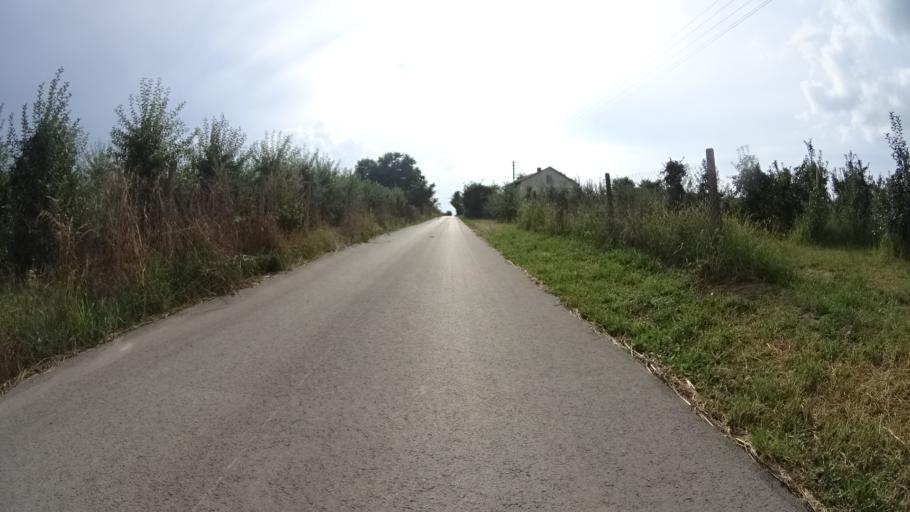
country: PL
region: Masovian Voivodeship
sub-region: Powiat grojecki
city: Goszczyn
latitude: 51.7046
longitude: 20.8408
